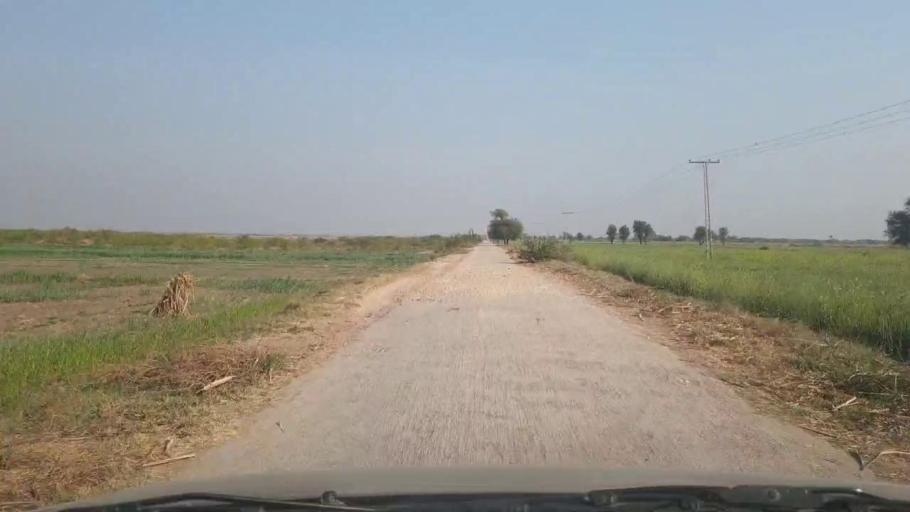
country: PK
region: Sindh
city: Digri
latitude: 25.2421
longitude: 69.1852
